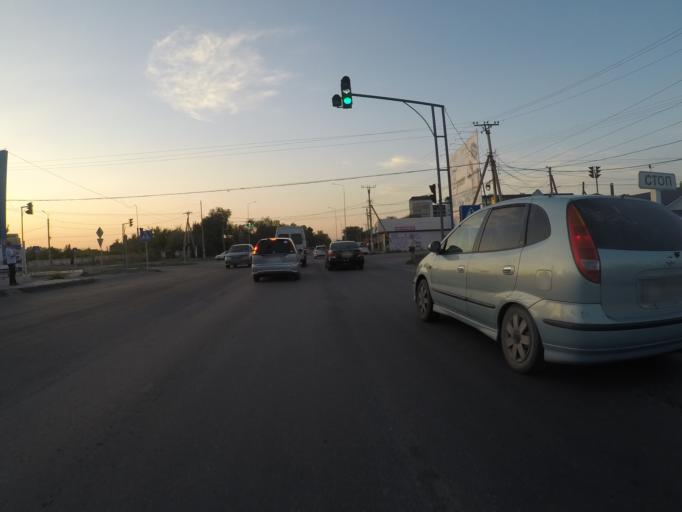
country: KG
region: Chuy
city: Lebedinovka
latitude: 42.8122
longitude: 74.6456
